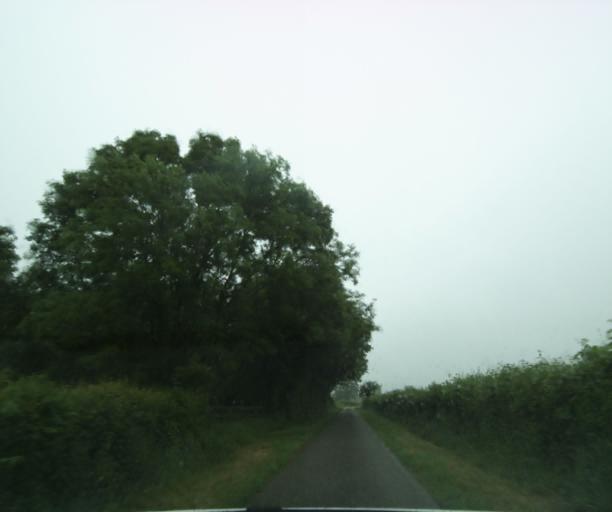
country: FR
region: Bourgogne
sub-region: Departement de Saone-et-Loire
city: Charolles
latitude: 46.3952
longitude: 4.2231
